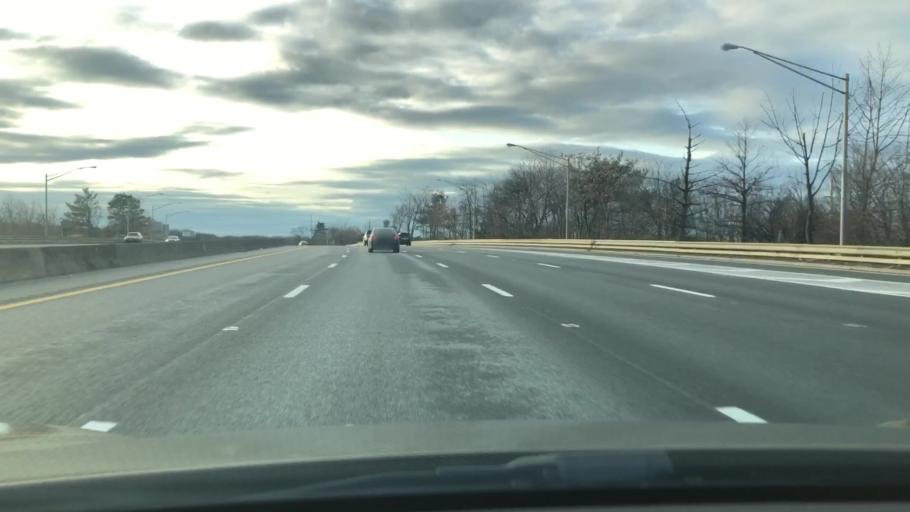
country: US
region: New Jersey
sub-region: Passaic County
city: Singac
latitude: 40.8995
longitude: -74.2338
